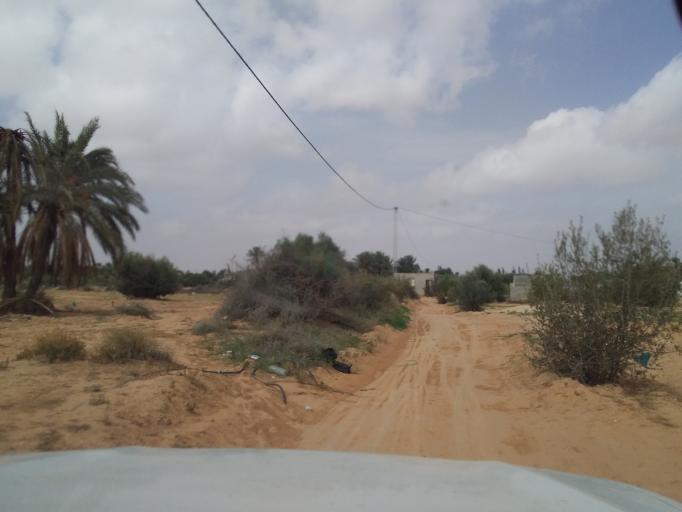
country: TN
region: Qabis
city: Gabes
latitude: 33.6262
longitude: 10.2962
